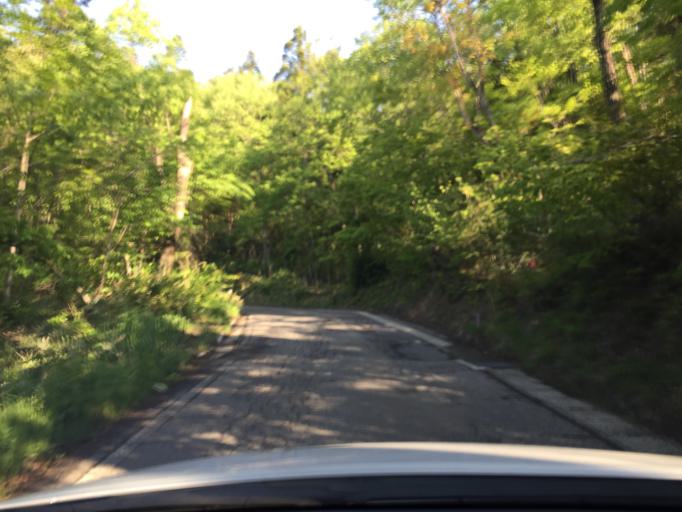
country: JP
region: Fukushima
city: Kitakata
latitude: 37.6692
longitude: 139.8402
